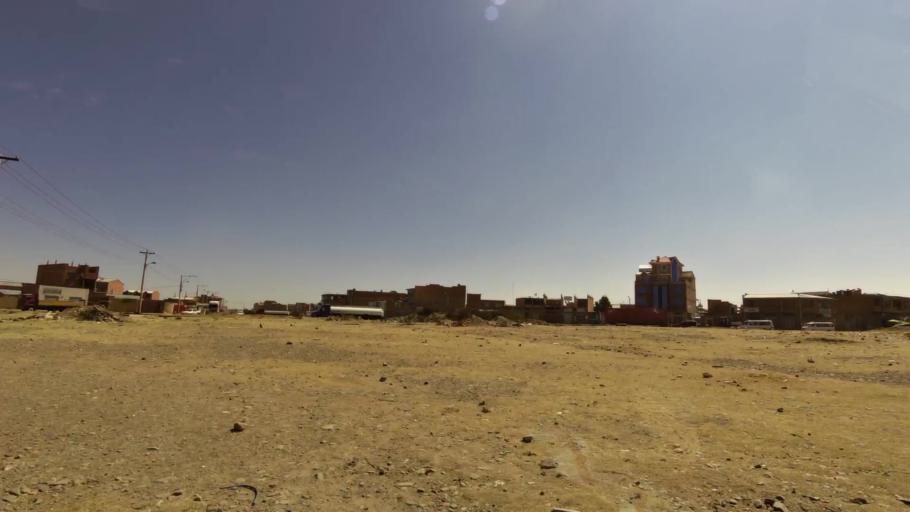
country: BO
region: La Paz
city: La Paz
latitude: -16.5528
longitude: -68.1849
